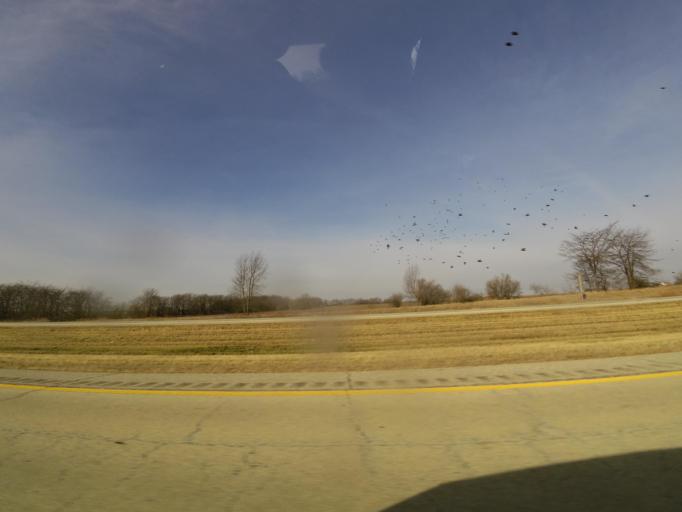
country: US
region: Illinois
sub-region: Macon County
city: Warrensburg
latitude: 39.8881
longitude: -89.0150
